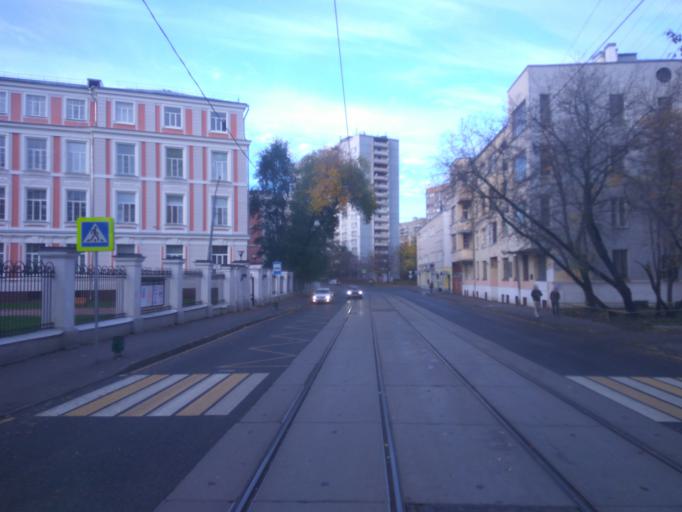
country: RU
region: Moscow
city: Mar'ina Roshcha
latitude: 55.7873
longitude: 37.6088
